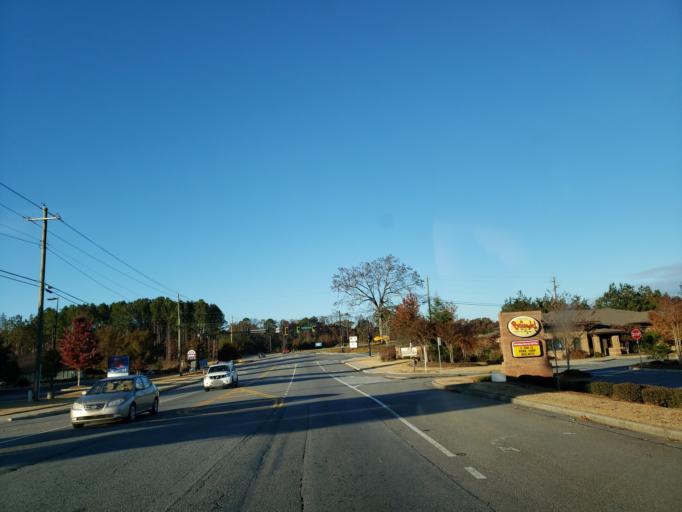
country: US
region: Georgia
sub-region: Cherokee County
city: Holly Springs
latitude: 34.1780
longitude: -84.4200
